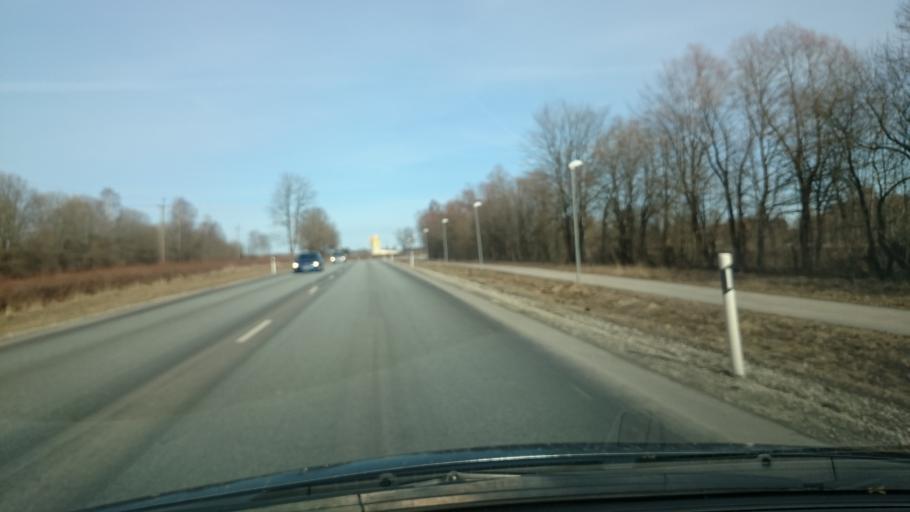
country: EE
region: Jaervamaa
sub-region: Paide linn
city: Paide
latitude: 58.9092
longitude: 25.5860
